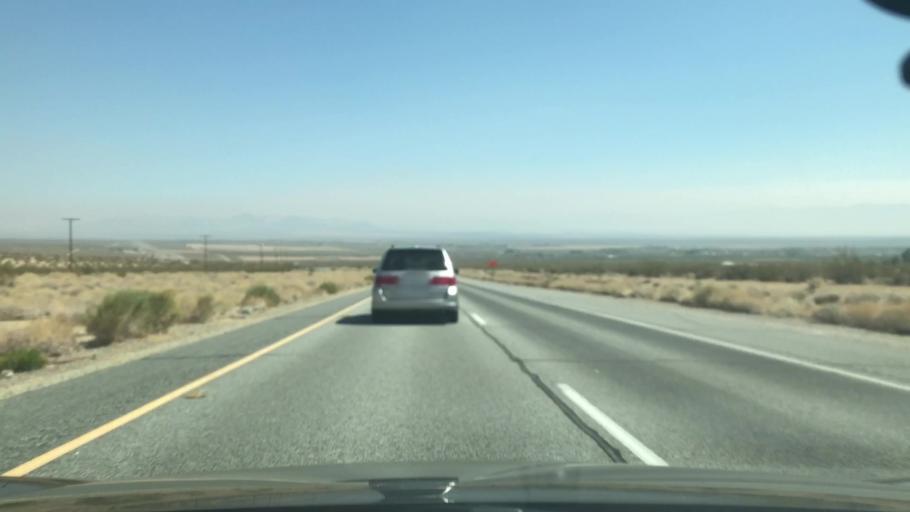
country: US
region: California
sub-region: Kern County
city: Inyokern
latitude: 35.6761
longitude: -117.8684
